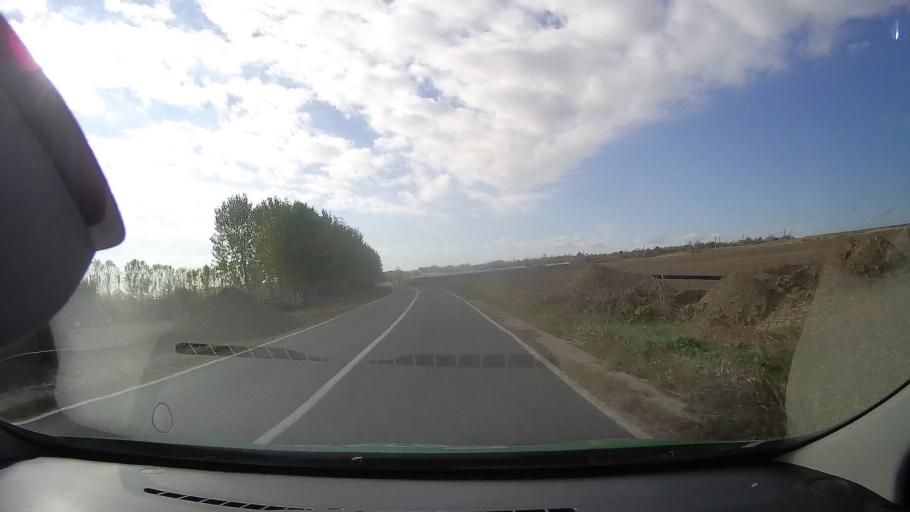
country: RO
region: Tulcea
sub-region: Comuna Sarichioi
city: Sarichioi
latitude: 44.9594
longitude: 28.8584
